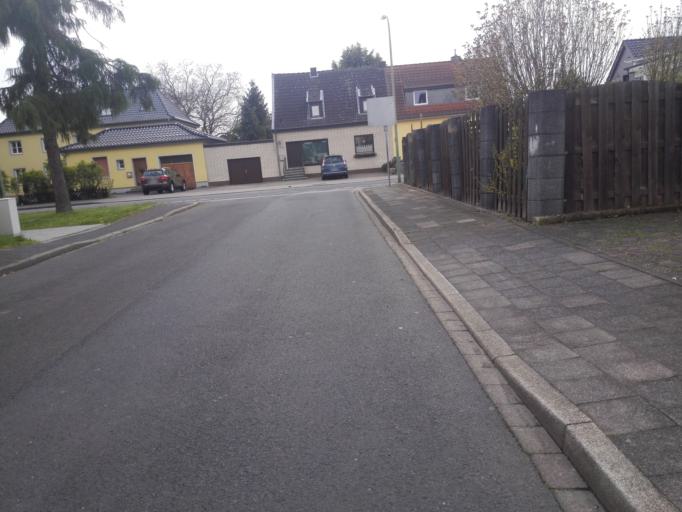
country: DE
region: North Rhine-Westphalia
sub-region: Regierungsbezirk Koln
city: Dueren
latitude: 50.8397
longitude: 6.4903
